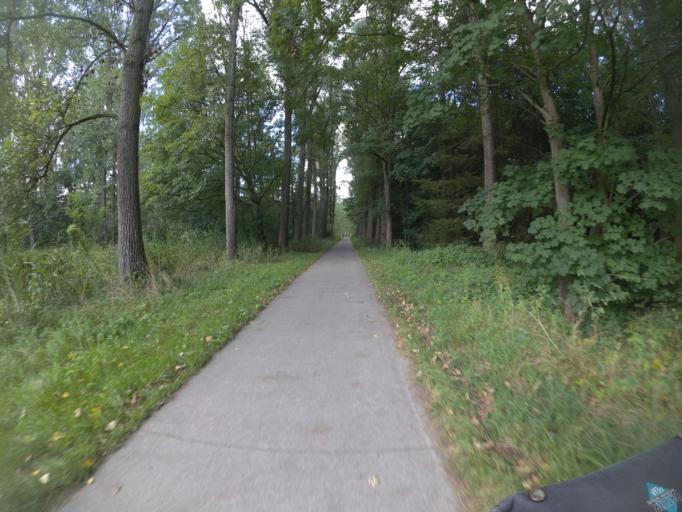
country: NL
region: North Brabant
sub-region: Gemeente Schijndel
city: Schijndel
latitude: 51.6333
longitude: 5.4674
